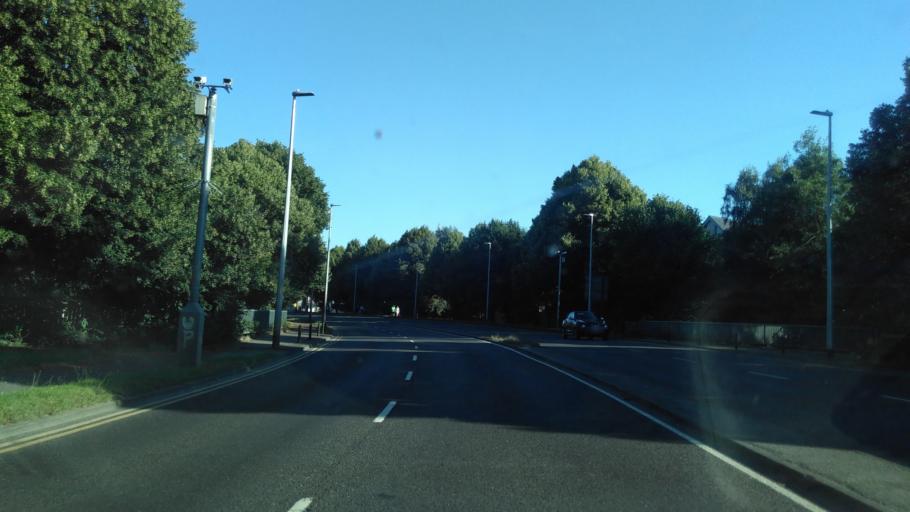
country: GB
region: England
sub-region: Kent
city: Canterbury
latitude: 51.2772
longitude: 1.0726
